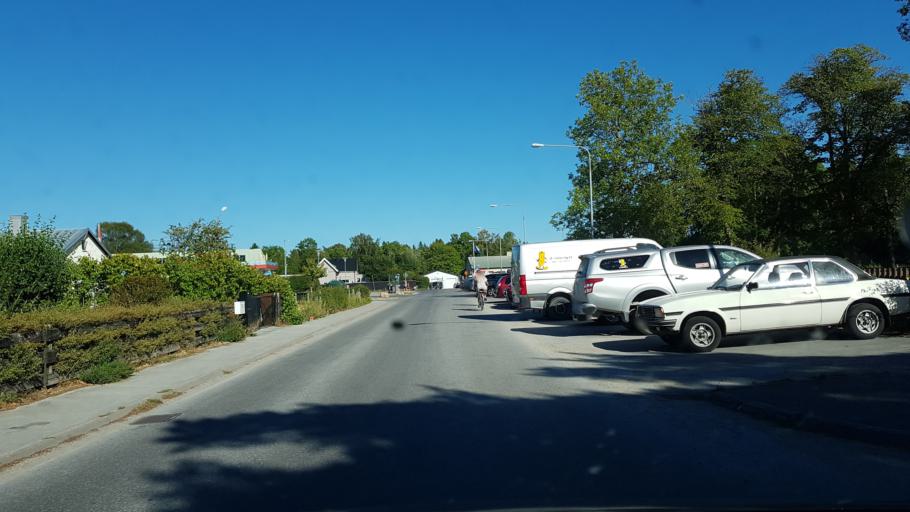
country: SE
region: Gotland
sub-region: Gotland
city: Vibble
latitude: 57.6015
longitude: 18.2496
